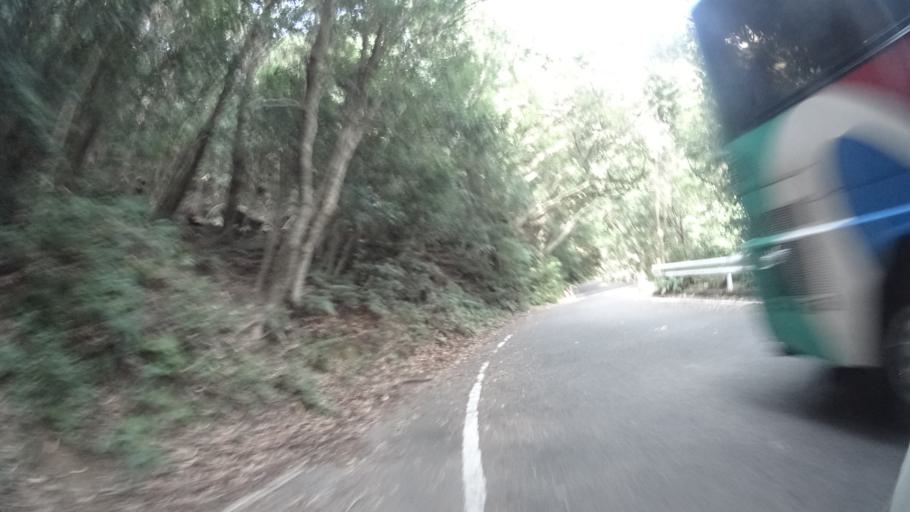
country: JP
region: Kagoshima
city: Nishinoomote
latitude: 30.3401
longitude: 130.3942
